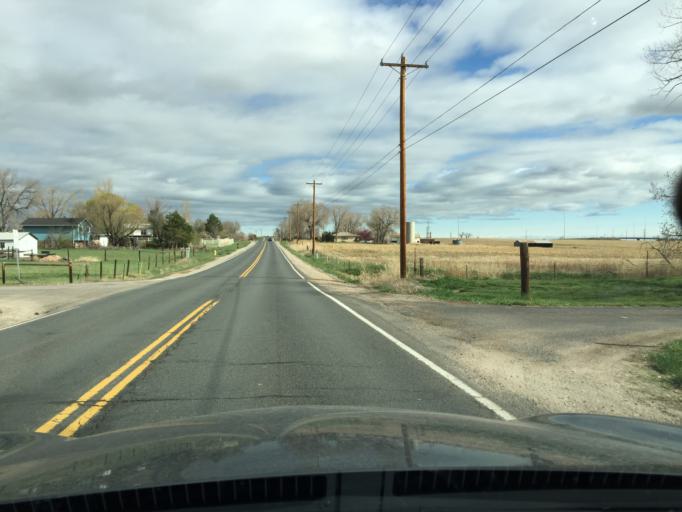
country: US
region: Colorado
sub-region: Adams County
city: Northglenn
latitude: 39.9754
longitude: -104.9972
